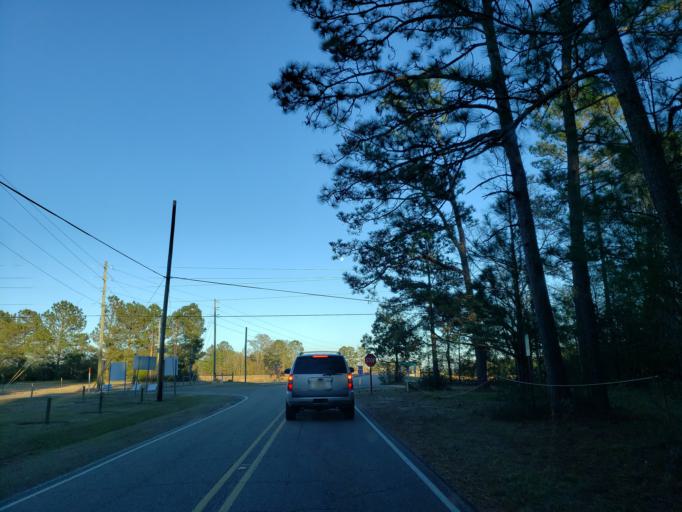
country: US
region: Mississippi
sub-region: Forrest County
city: Glendale
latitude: 31.4311
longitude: -89.3212
